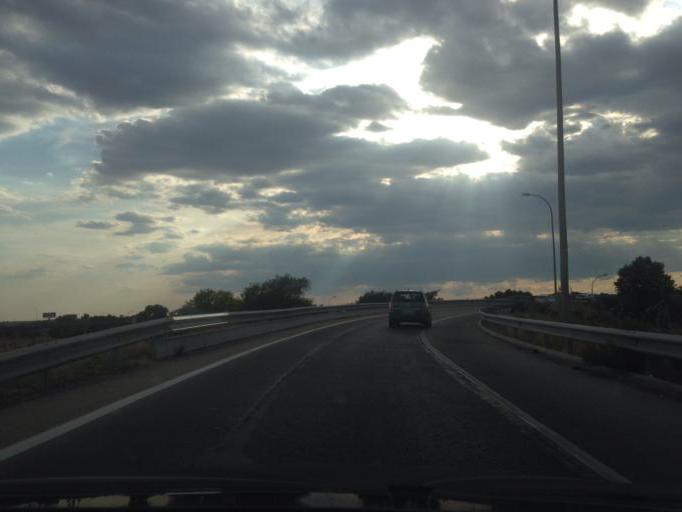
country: ES
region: Madrid
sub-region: Provincia de Madrid
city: Torrejon de Ardoz
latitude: 40.4662
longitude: -3.4833
